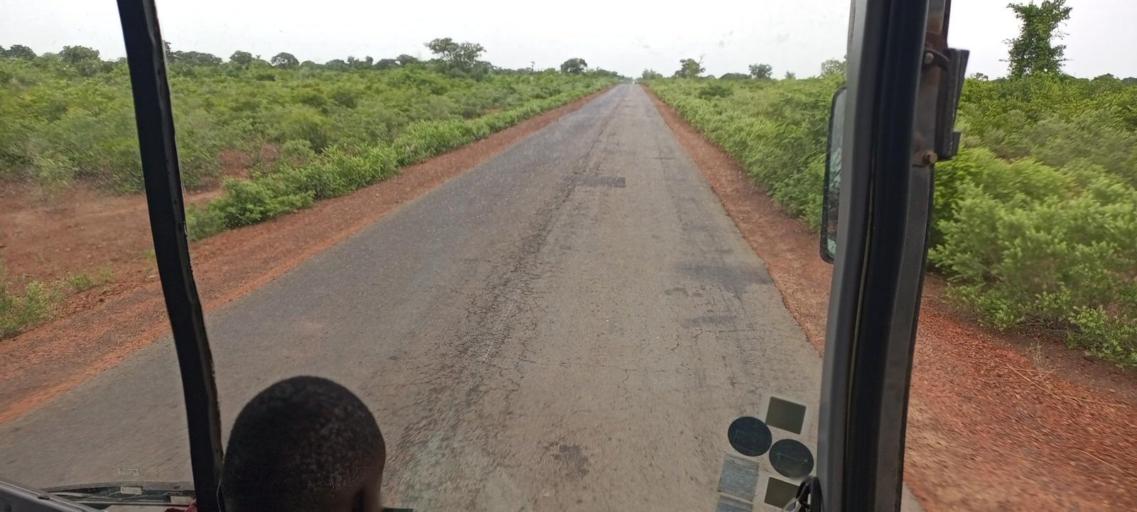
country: ML
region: Sikasso
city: Koutiala
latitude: 12.5627
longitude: -5.5949
